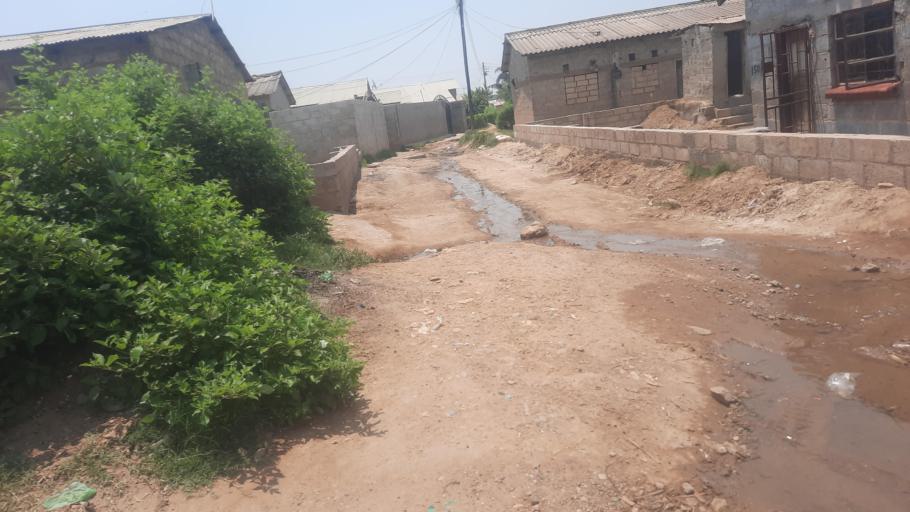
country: ZM
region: Lusaka
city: Lusaka
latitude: -15.4012
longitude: 28.3739
